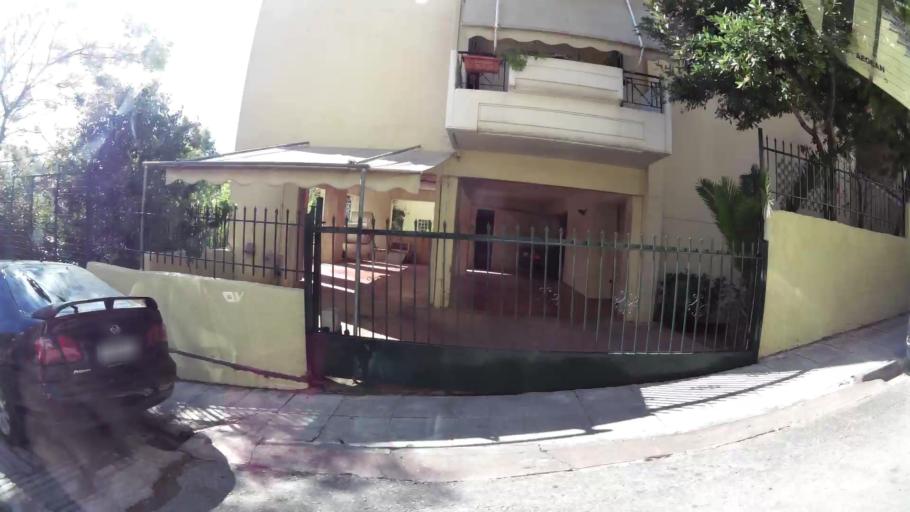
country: GR
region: Attica
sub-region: Nomarchia Athinas
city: Metamorfosi
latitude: 38.0655
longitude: 23.7734
